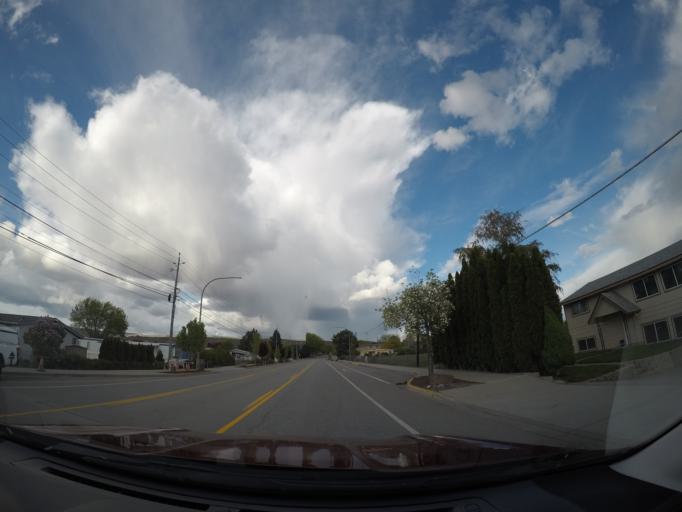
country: US
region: Washington
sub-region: Douglas County
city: East Wenatchee
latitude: 47.4179
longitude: -120.2856
